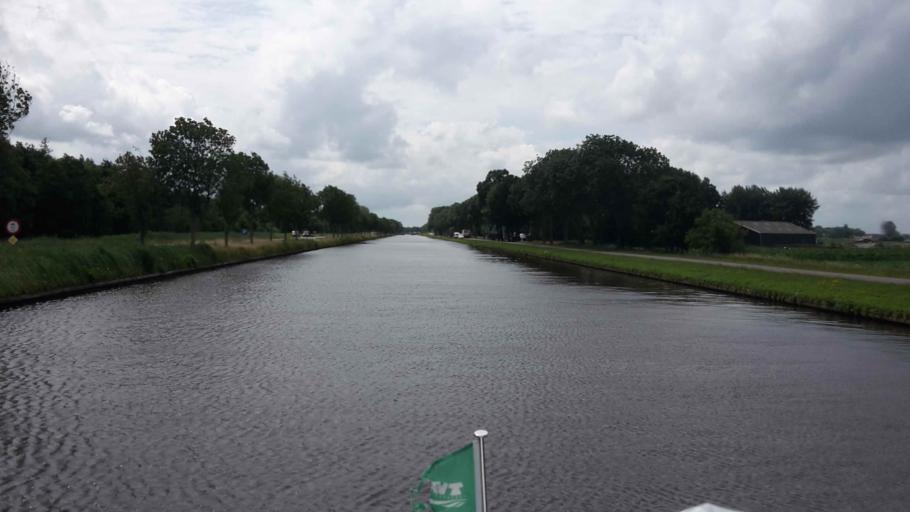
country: NL
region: Overijssel
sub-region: Gemeente Steenwijkerland
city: Giethoorn
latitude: 52.7520
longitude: 6.0785
